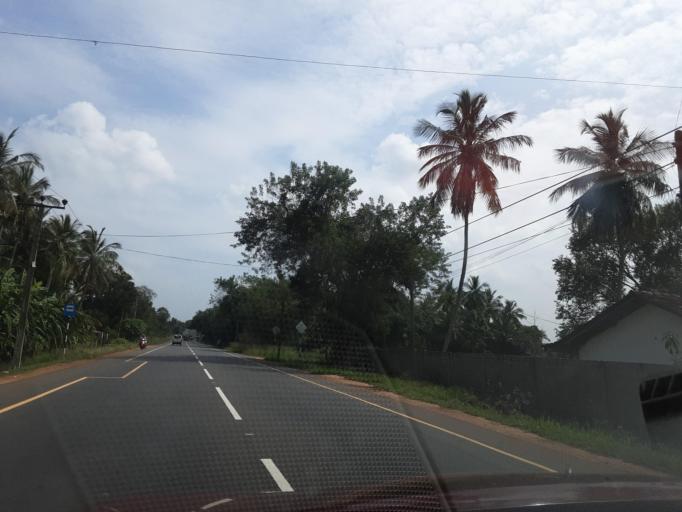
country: LK
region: North Central
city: Anuradhapura
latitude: 8.5042
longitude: 80.5093
